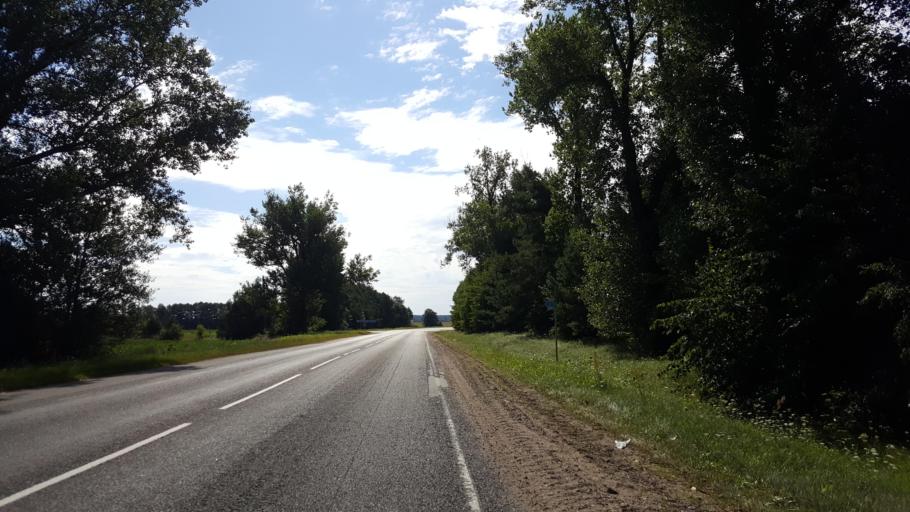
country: BY
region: Brest
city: Kamyanyets
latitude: 52.3731
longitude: 23.8800
